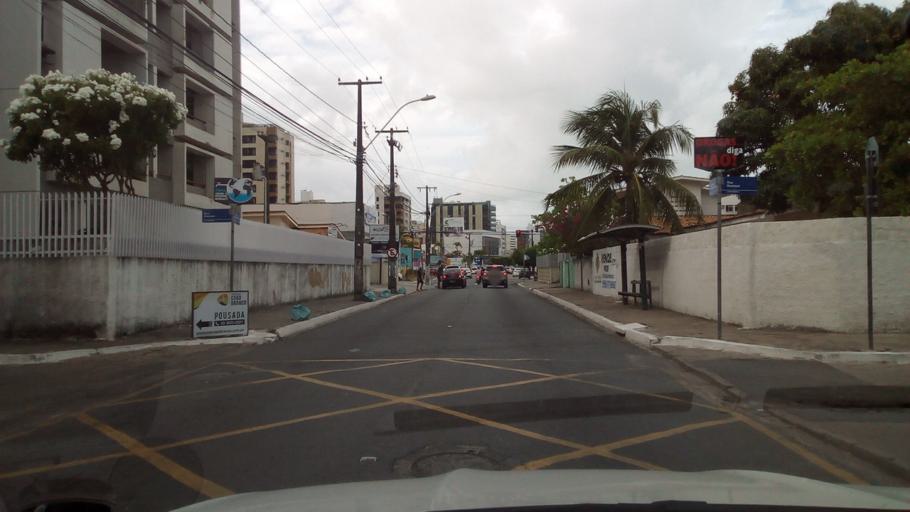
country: BR
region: Paraiba
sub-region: Joao Pessoa
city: Joao Pessoa
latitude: -7.1257
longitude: -34.8260
